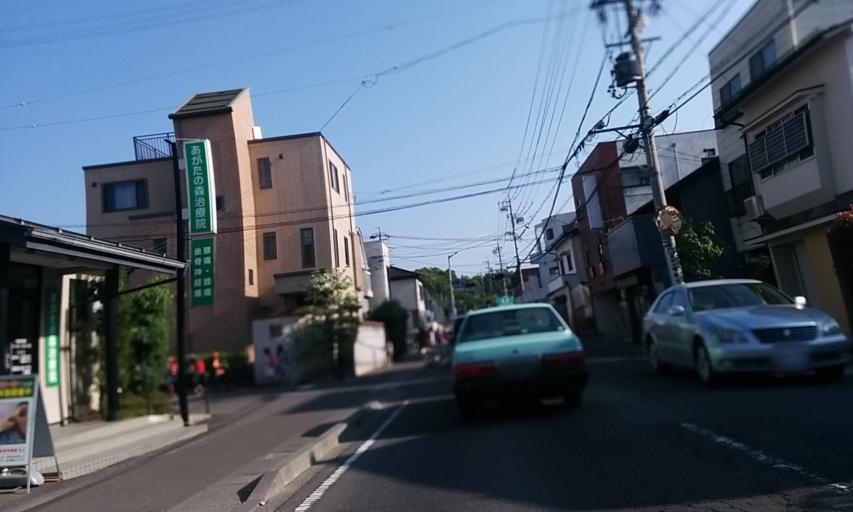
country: JP
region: Nagano
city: Matsumoto
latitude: 36.2295
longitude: 137.9818
